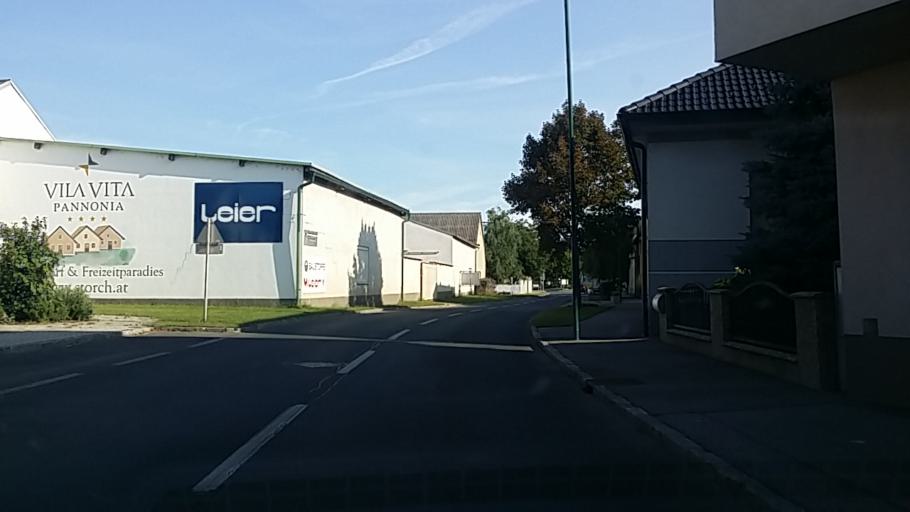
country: AT
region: Burgenland
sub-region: Politischer Bezirk Neusiedl am See
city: Pamhagen
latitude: 47.6978
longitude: 16.9104
